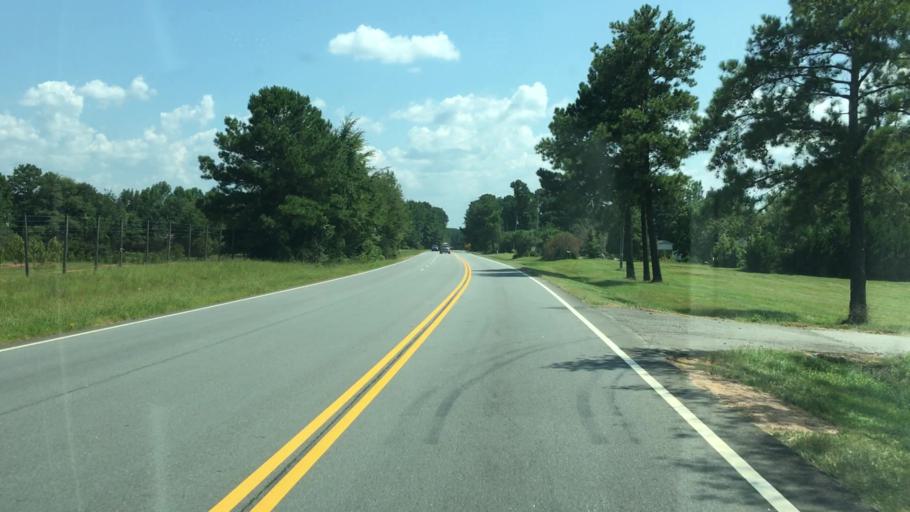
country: US
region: Georgia
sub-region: Oconee County
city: Watkinsville
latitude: 33.7435
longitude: -83.4316
